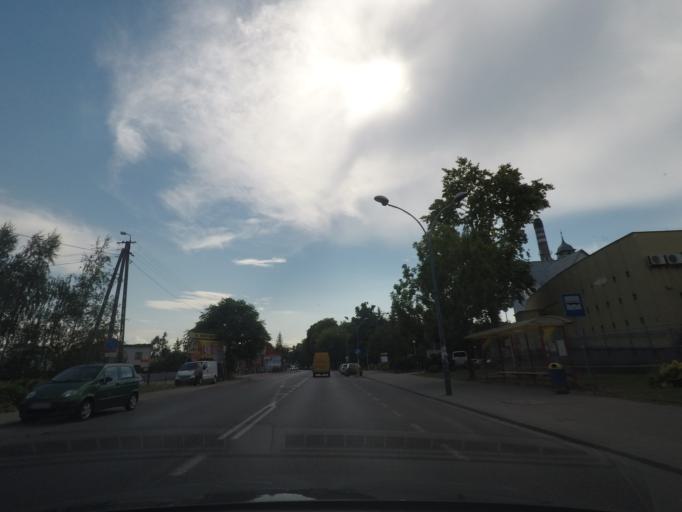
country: PL
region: Lesser Poland Voivodeship
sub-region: Powiat oswiecimski
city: Brzeszcze
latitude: 49.9860
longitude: 19.1579
